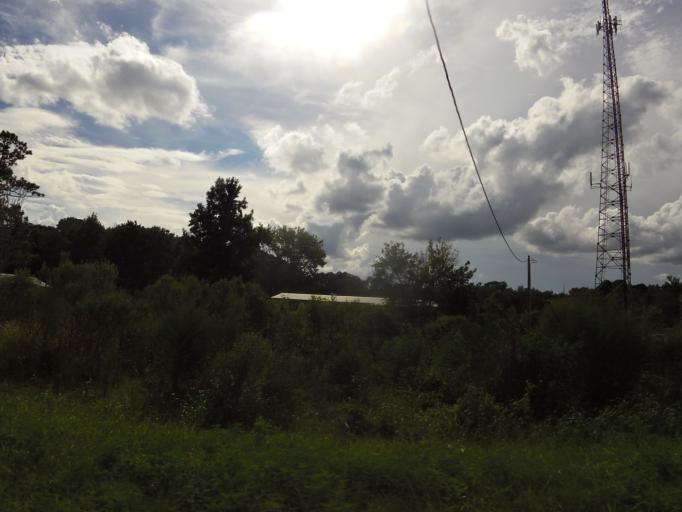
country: US
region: Florida
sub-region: Clay County
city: Green Cove Springs
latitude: 29.9687
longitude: -81.6933
